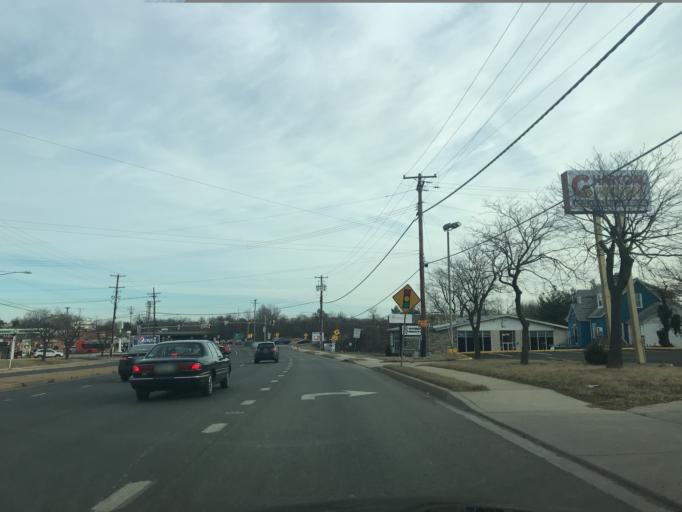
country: US
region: Maryland
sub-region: Prince George's County
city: Marlow Heights
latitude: 38.8297
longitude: -76.9418
